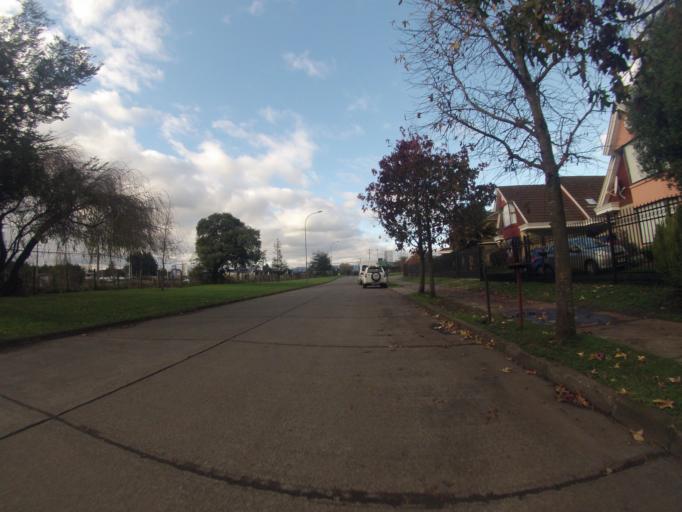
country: CL
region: Araucania
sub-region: Provincia de Cautin
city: Temuco
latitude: -38.7360
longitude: -72.6414
